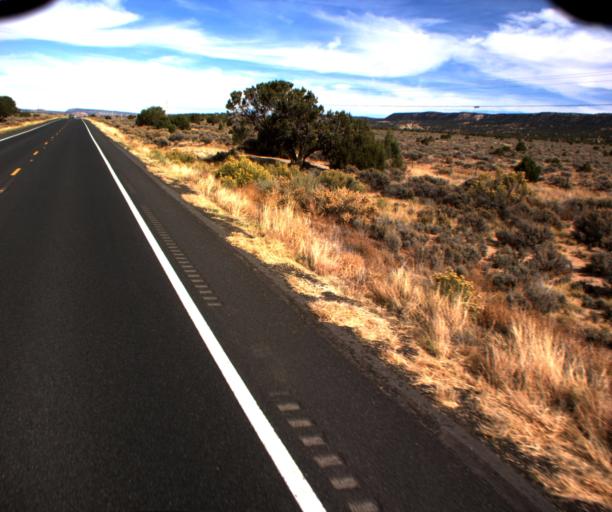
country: US
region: Arizona
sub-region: Navajo County
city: Kayenta
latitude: 36.5093
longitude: -110.6047
